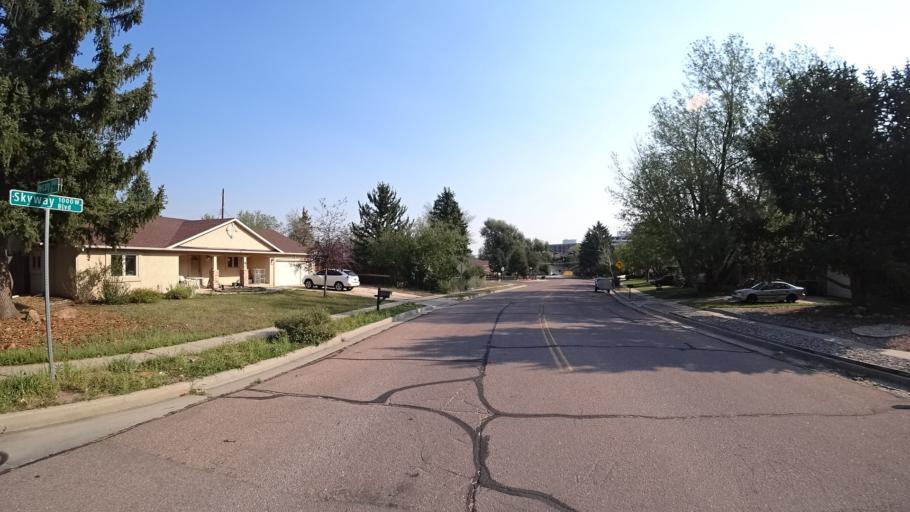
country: US
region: Colorado
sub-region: El Paso County
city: Colorado Springs
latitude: 38.8056
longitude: -104.8471
